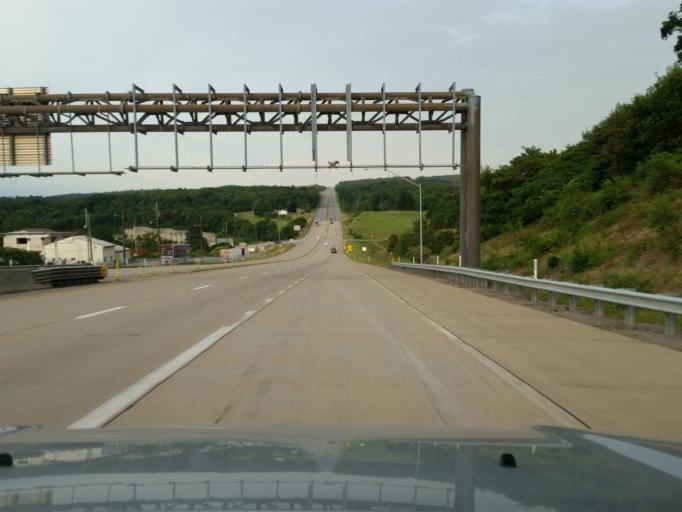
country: US
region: Pennsylvania
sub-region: Indiana County
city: Black Lick
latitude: 40.4468
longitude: -79.2108
